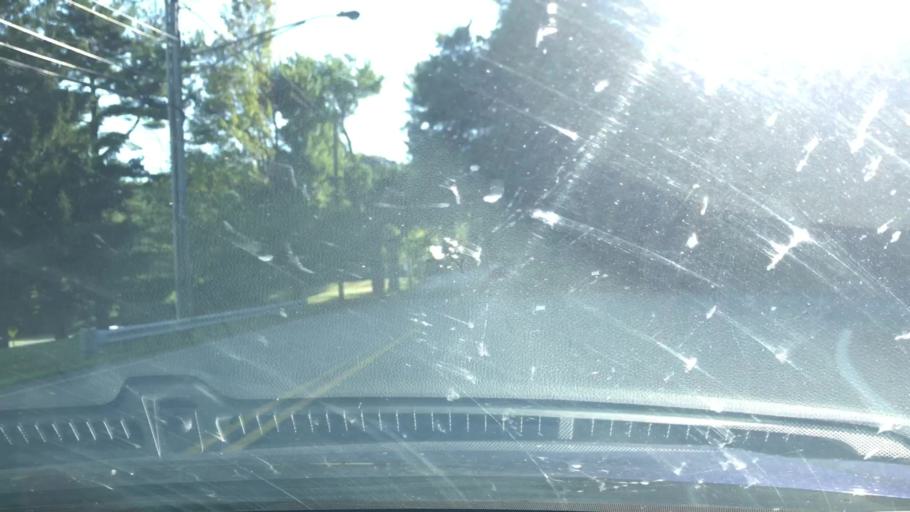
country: US
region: New Jersey
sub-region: Bergen County
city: Cresskill
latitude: 40.9419
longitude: -73.9445
